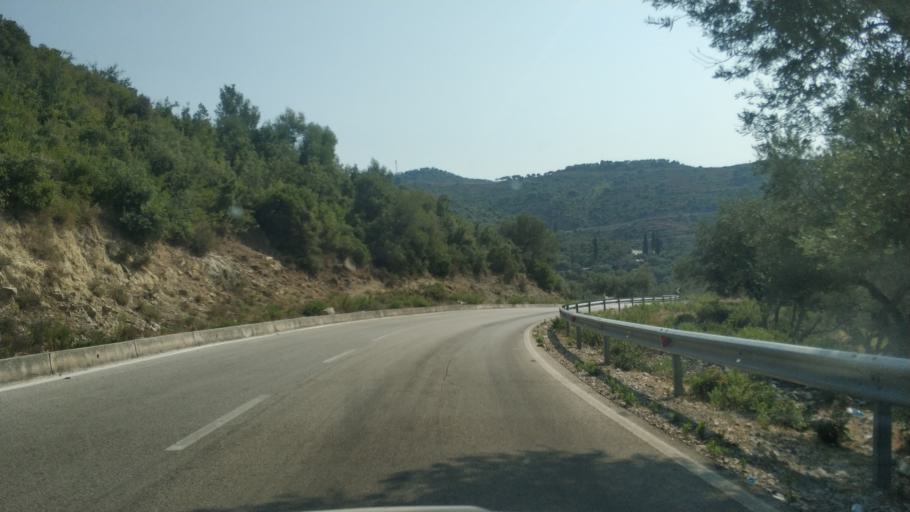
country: AL
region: Vlore
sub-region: Rrethi i Sarandes
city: Lukove
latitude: 40.0106
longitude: 19.9025
